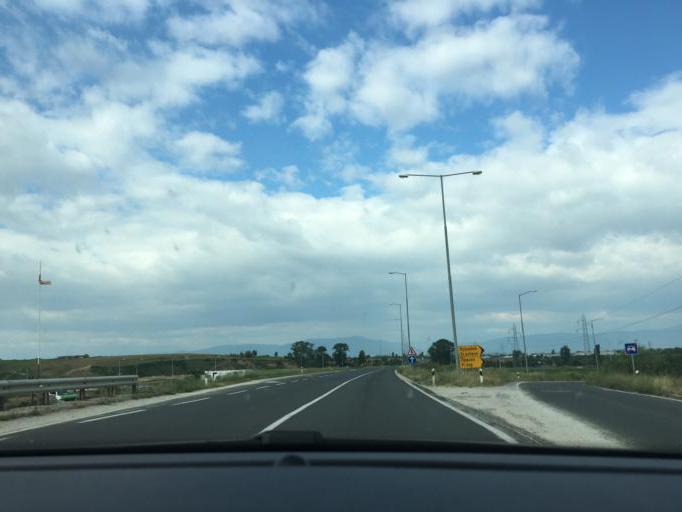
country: MK
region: Prilep
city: Prilep
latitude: 41.3308
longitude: 21.5597
